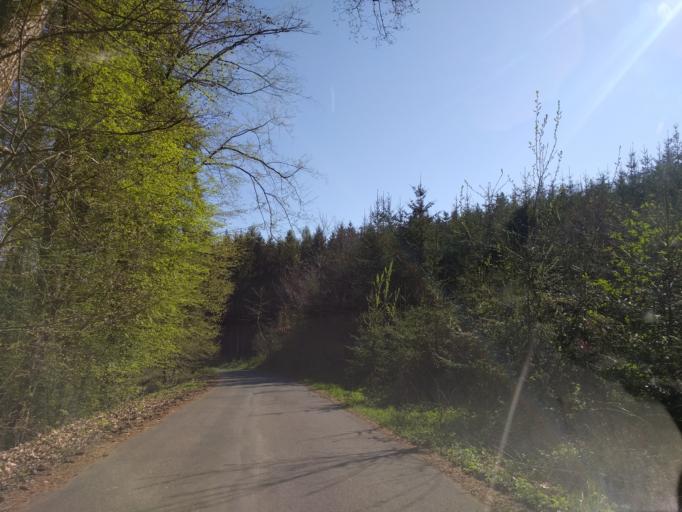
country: CZ
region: Central Bohemia
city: Kostelec nad Cernymi Lesy
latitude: 50.0221
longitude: 14.8072
